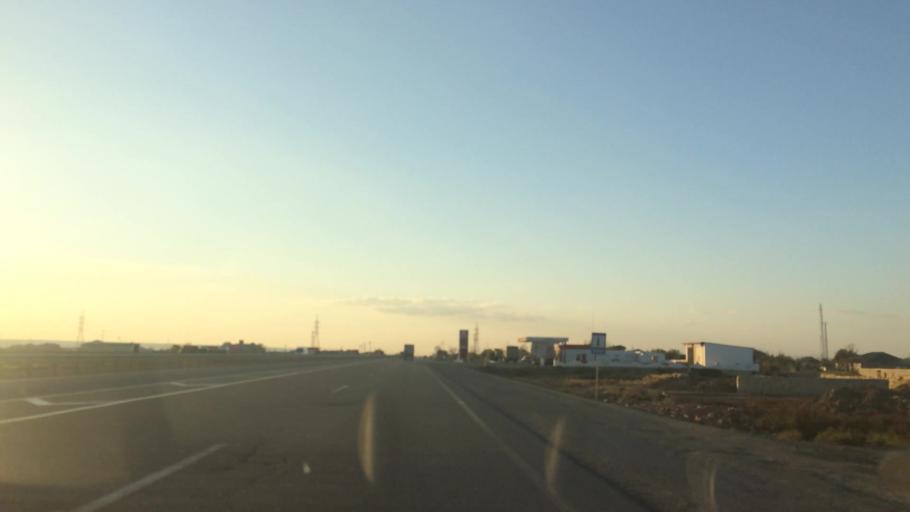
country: AZ
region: Baki
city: Qobustan
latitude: 39.9678
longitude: 49.2711
